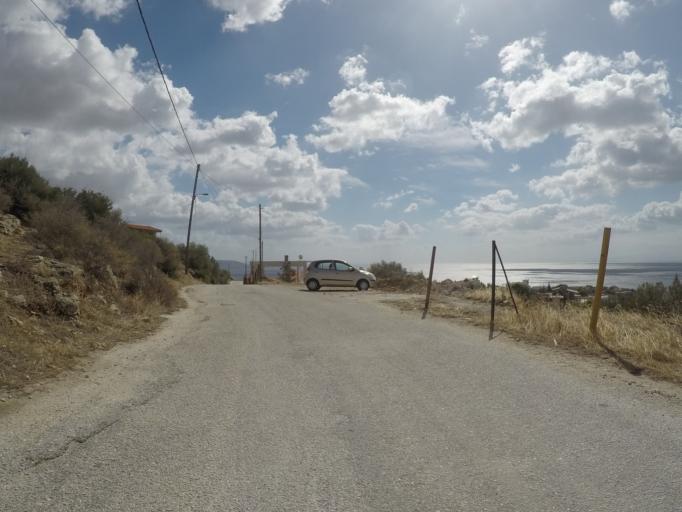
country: GR
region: Attica
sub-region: Nomarchia Anatolikis Attikis
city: Agios Dimitrios Kropias
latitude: 37.8002
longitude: 23.8784
